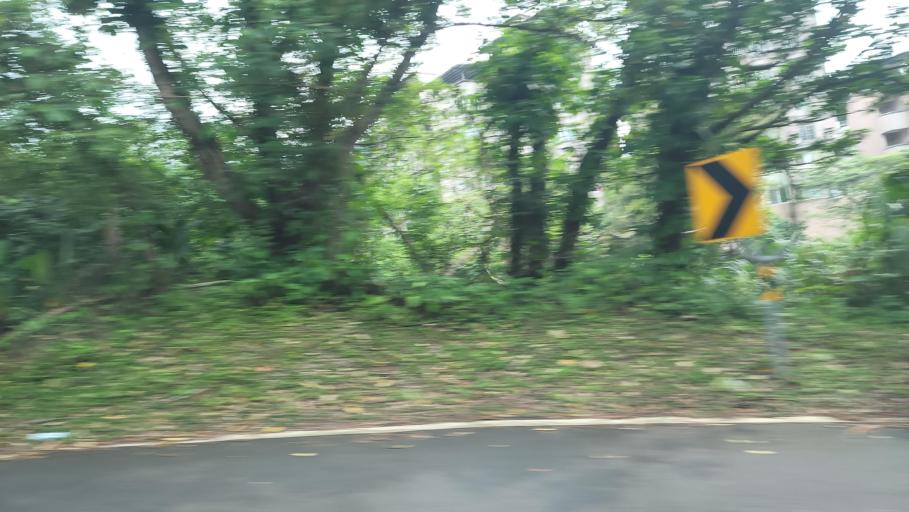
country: TW
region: Taiwan
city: Daxi
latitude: 24.9095
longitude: 121.3931
